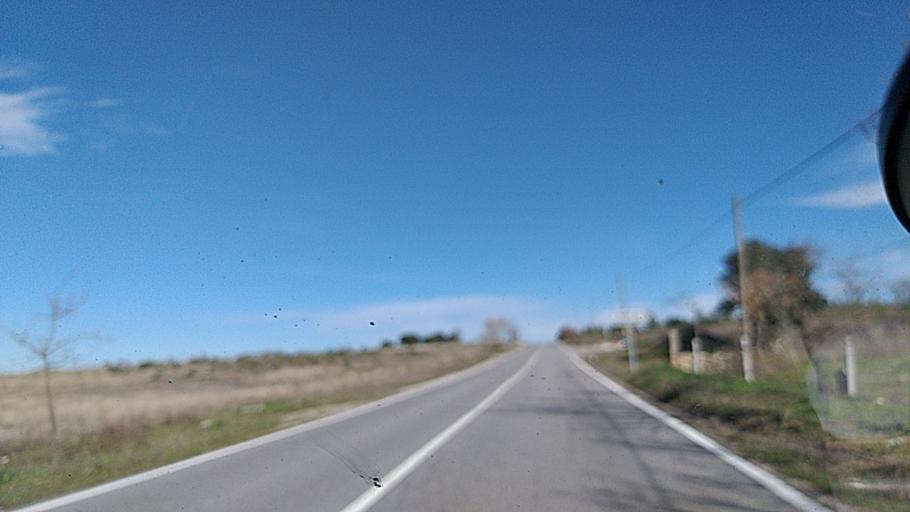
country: ES
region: Castille and Leon
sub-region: Provincia de Salamanca
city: Fuentes de Onoro
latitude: 40.6146
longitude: -6.8781
